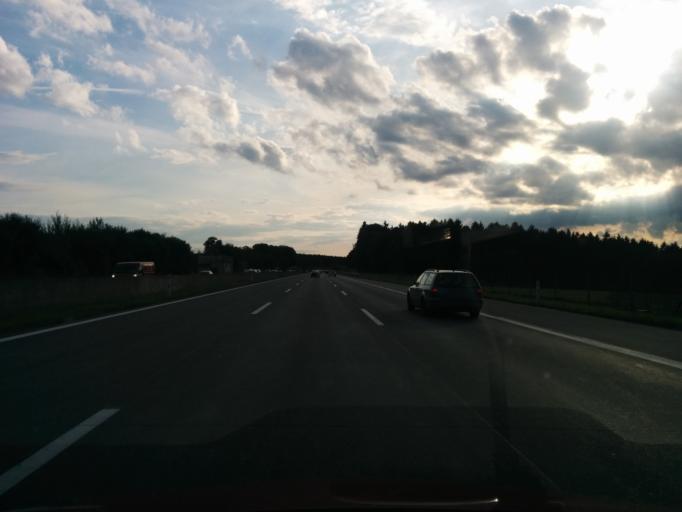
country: AT
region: Lower Austria
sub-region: Politischer Bezirk Amstetten
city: Zeillern
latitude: 48.1238
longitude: 14.8161
